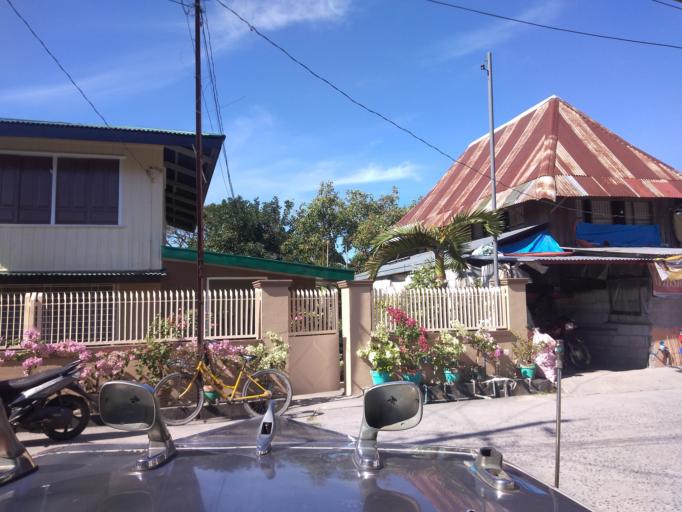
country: PH
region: Central Luzon
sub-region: Province of Pampanga
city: Santa Rita
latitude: 14.9932
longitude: 120.6117
